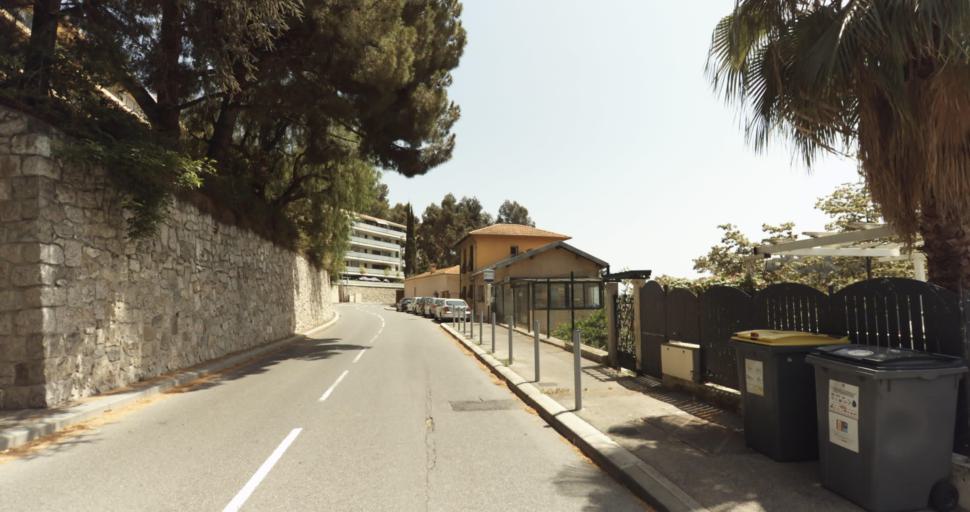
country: FR
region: Provence-Alpes-Cote d'Azur
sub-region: Departement des Alpes-Maritimes
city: Roquebrune-Cap-Martin
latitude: 43.7726
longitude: 7.4775
